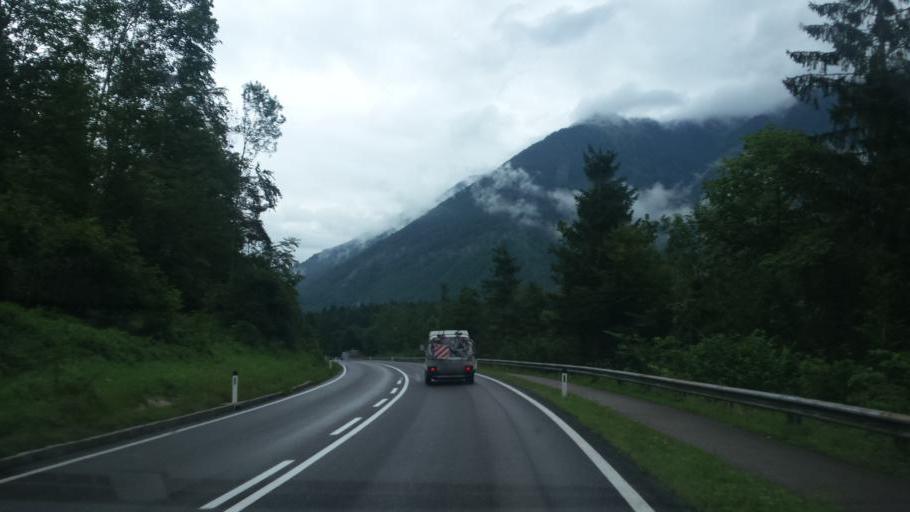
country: AT
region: Upper Austria
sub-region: Politischer Bezirk Gmunden
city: Bad Ischl
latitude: 47.7458
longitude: 13.6826
